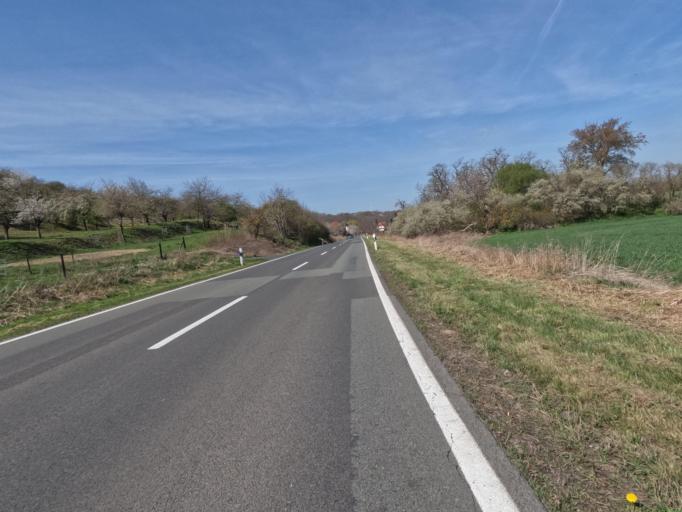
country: DE
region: Saxony-Anhalt
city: Wettin
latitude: 51.5759
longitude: 11.7790
